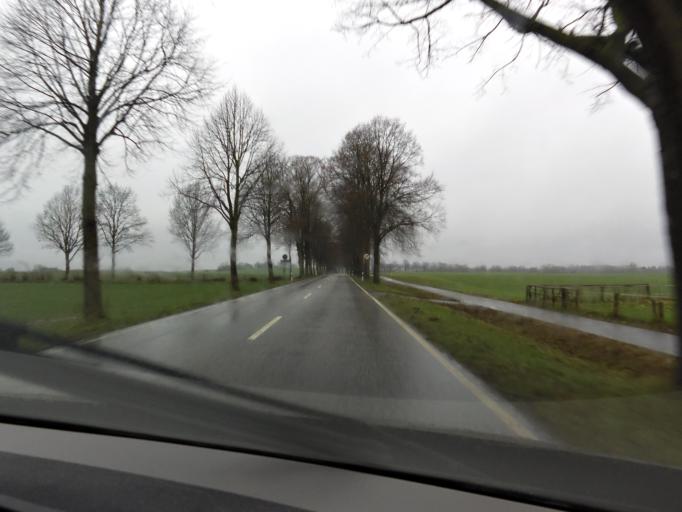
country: DE
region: Schleswig-Holstein
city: Ziethen
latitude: 53.6921
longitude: 10.8367
